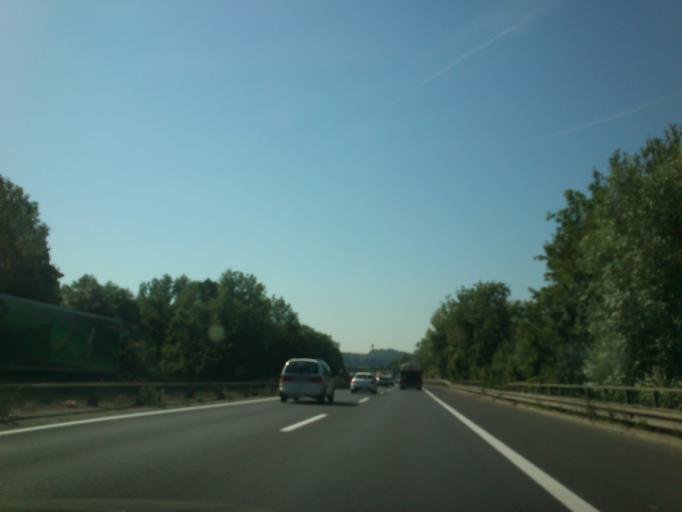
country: AT
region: Upper Austria
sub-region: Politischer Bezirk Linz-Land
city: Ansfelden
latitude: 48.2330
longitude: 14.2977
